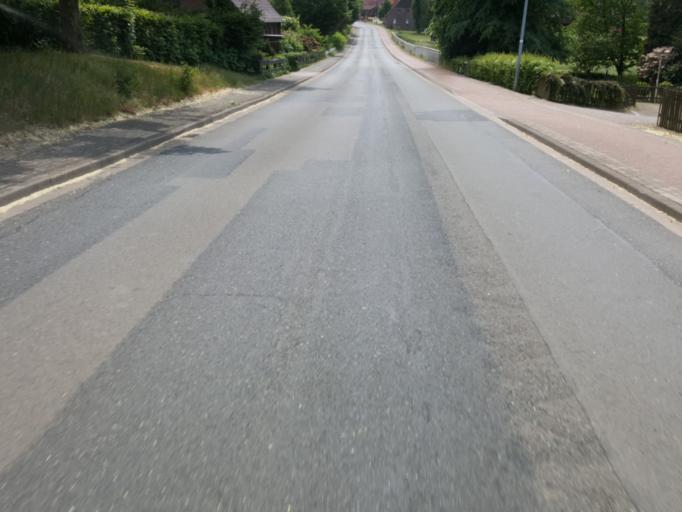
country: DE
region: Lower Saxony
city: Husum
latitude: 52.5693
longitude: 9.2494
